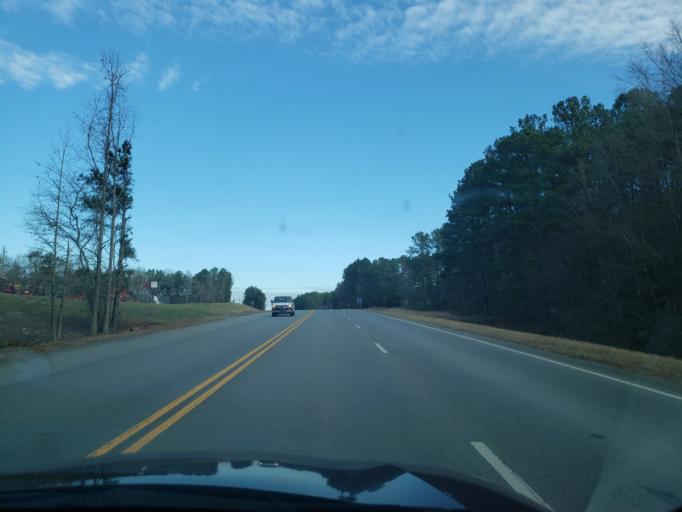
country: US
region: Alabama
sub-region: Randolph County
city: Wedowee
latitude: 33.4595
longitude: -85.5733
